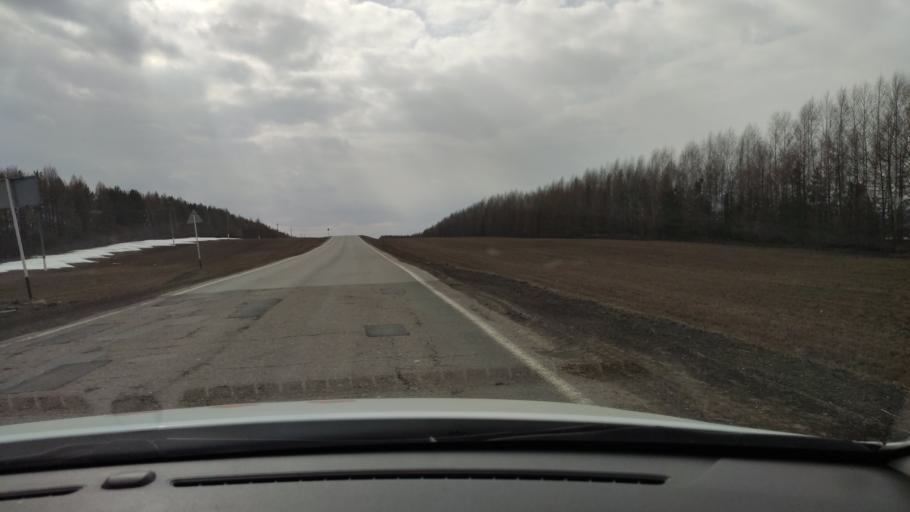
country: RU
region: Tatarstan
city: Vysokaya Gora
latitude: 56.2268
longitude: 49.2943
